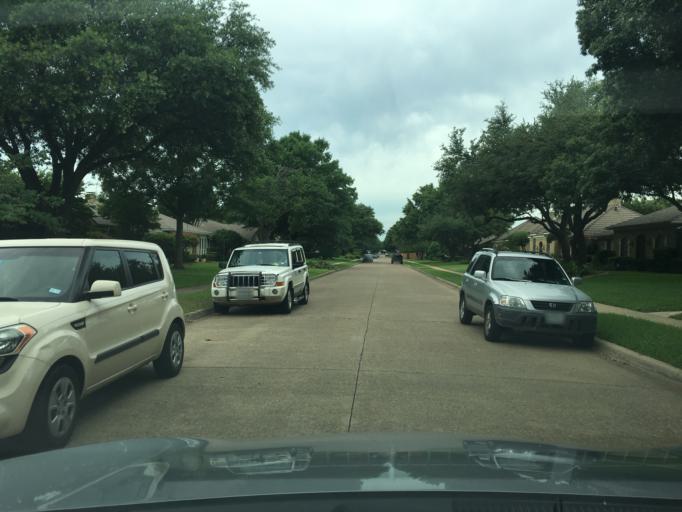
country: US
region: Texas
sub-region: Dallas County
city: Richardson
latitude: 32.9324
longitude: -96.7066
